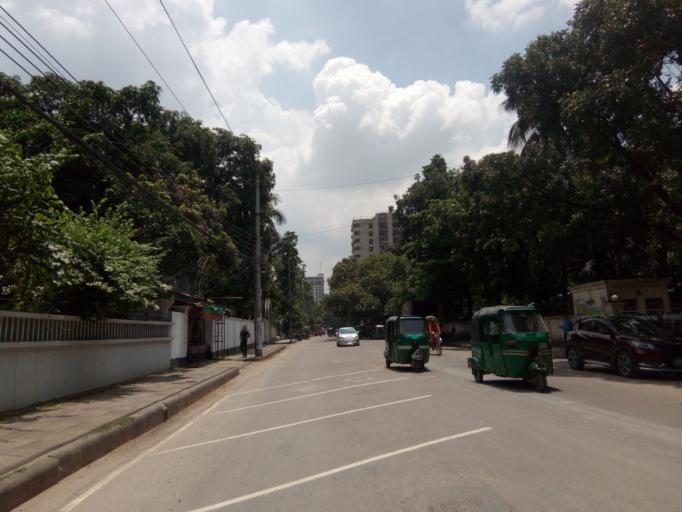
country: BD
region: Dhaka
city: Paltan
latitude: 23.7453
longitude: 90.4002
